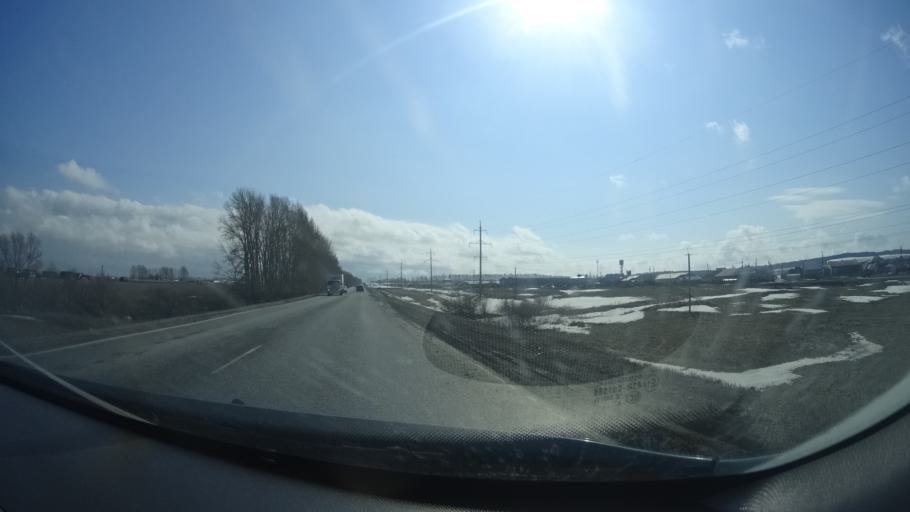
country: RU
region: Bashkortostan
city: Mikhaylovka
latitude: 54.8676
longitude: 55.7446
